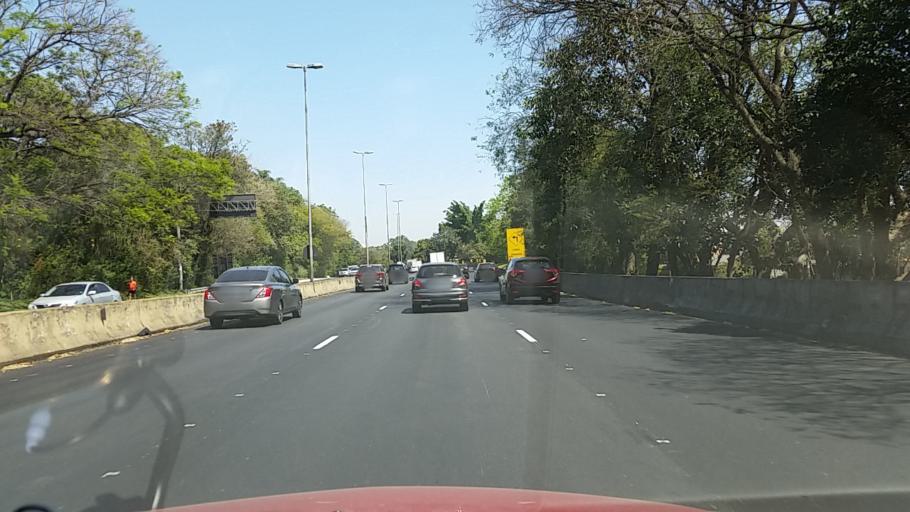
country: BR
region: Sao Paulo
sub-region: Osasco
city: Osasco
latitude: -23.5783
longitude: -46.7267
